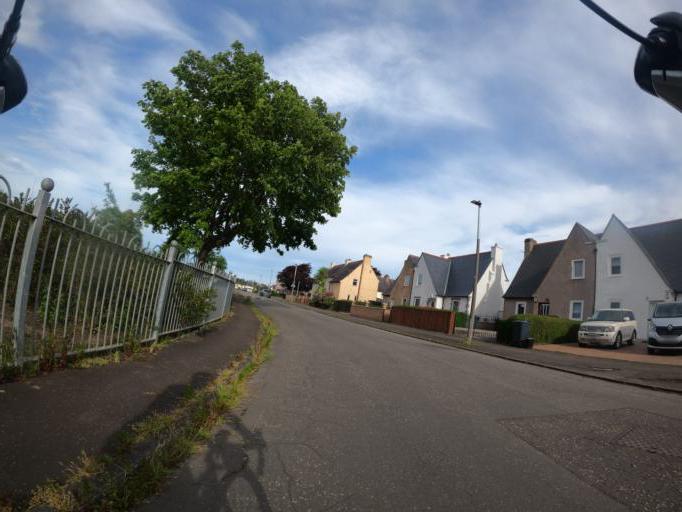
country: GB
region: Scotland
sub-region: Edinburgh
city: Edinburgh
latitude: 55.9739
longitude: -3.2197
